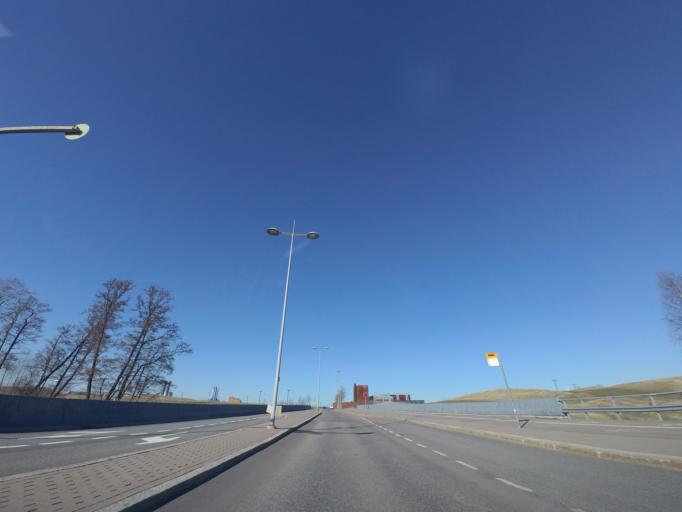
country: FI
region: Uusimaa
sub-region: Helsinki
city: Vantaa
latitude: 60.2106
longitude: 25.1635
